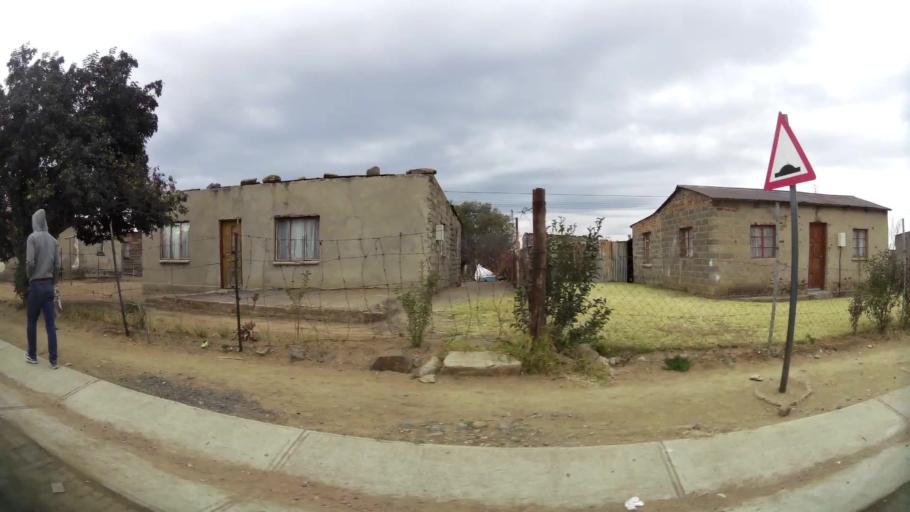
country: ZA
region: Orange Free State
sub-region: Fezile Dabi District Municipality
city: Kroonstad
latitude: -27.6487
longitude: 27.2043
